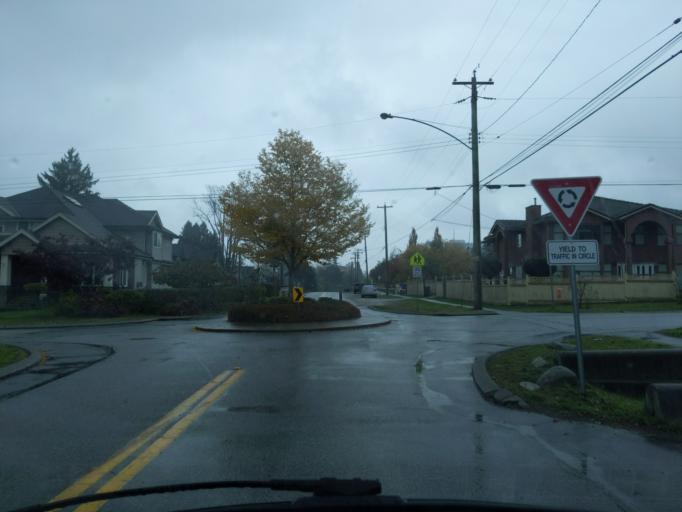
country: CA
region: British Columbia
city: New Westminster
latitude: 49.2009
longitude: -122.8605
